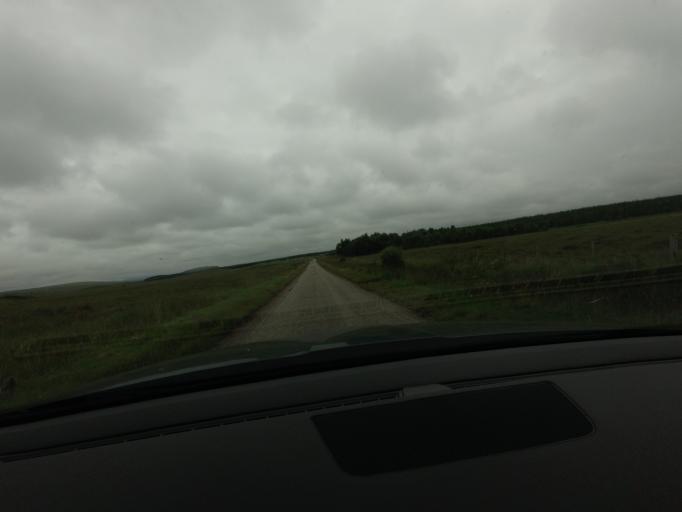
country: GB
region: Scotland
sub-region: Highland
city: Alness
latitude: 58.0945
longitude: -4.4211
